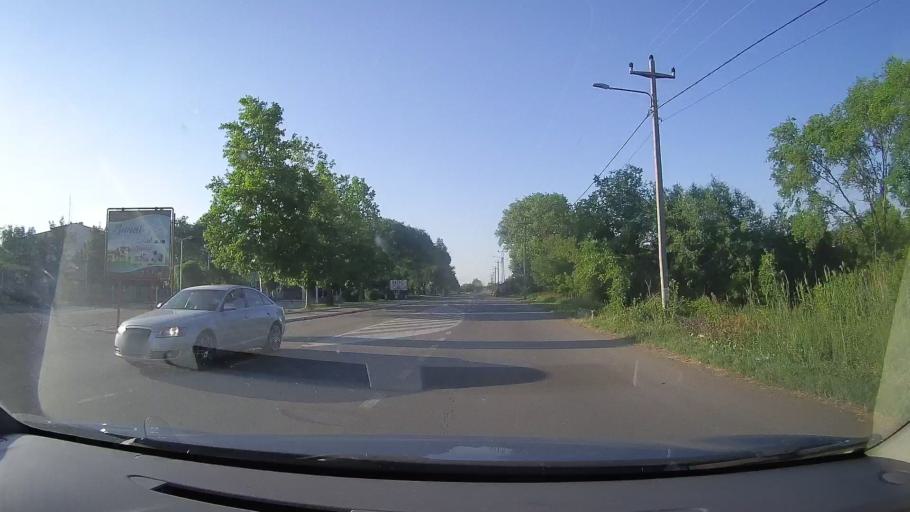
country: RS
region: Autonomna Pokrajina Vojvodina
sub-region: Juznobanatski Okrug
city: Vrsac
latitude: 45.1342
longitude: 21.2869
